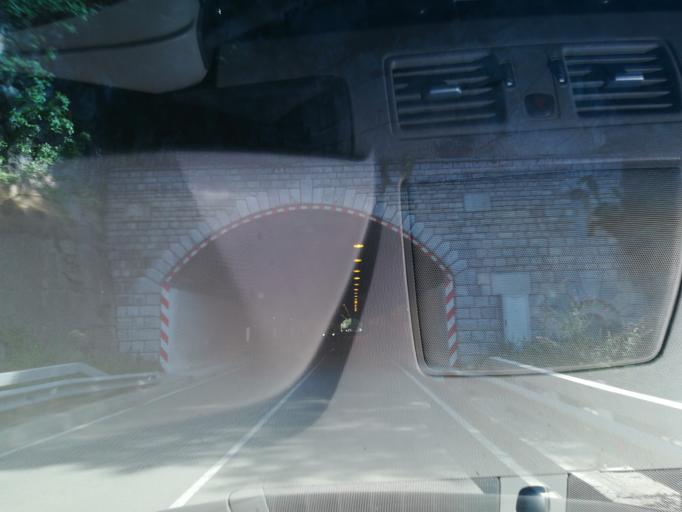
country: BG
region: Plovdiv
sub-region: Obshtina Asenovgrad
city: Asenovgrad
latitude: 41.9691
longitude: 24.8647
